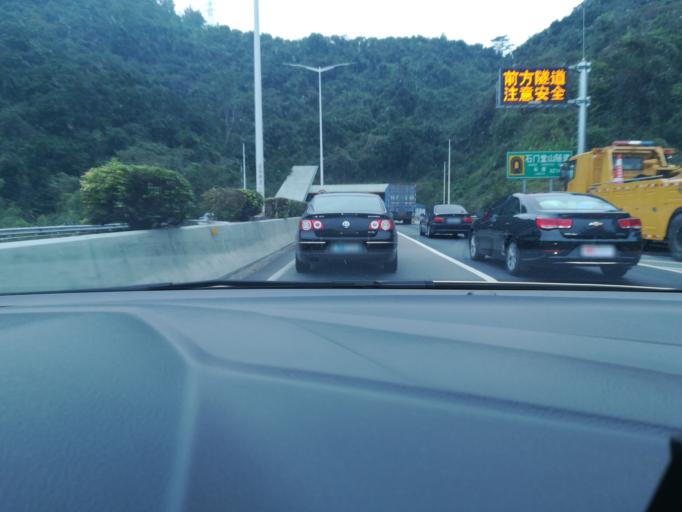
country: CN
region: Guangdong
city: Longdong
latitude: 23.2278
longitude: 113.3556
